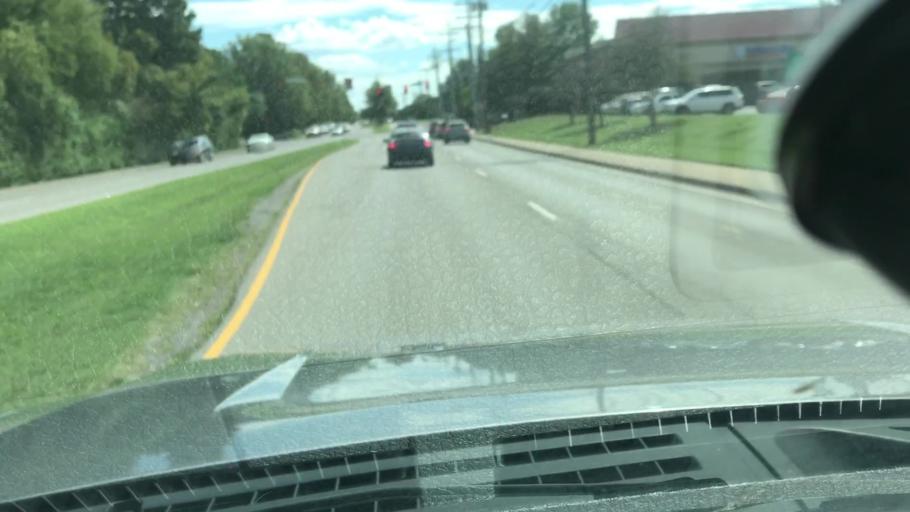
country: US
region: Tennessee
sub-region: Williamson County
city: Franklin
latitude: 35.9657
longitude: -86.8141
